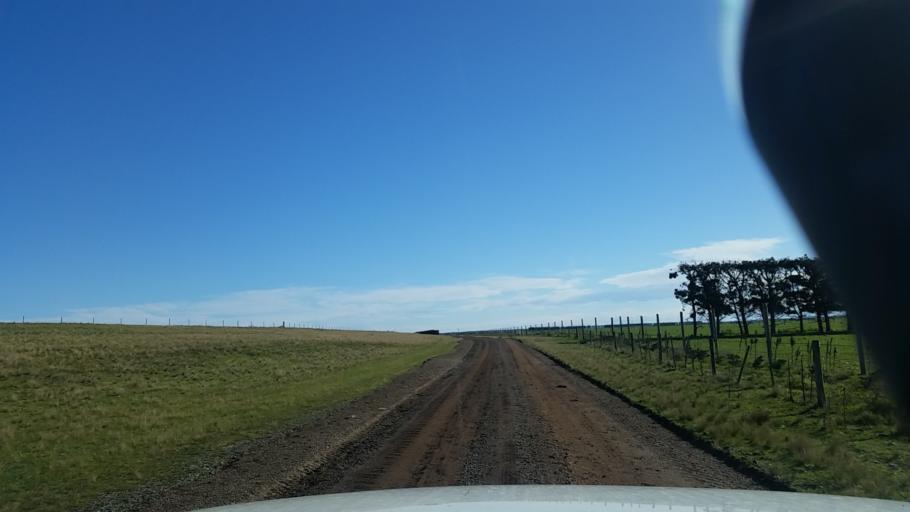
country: NZ
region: Canterbury
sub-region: Selwyn District
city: Lincoln
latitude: -43.8125
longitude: 172.6474
